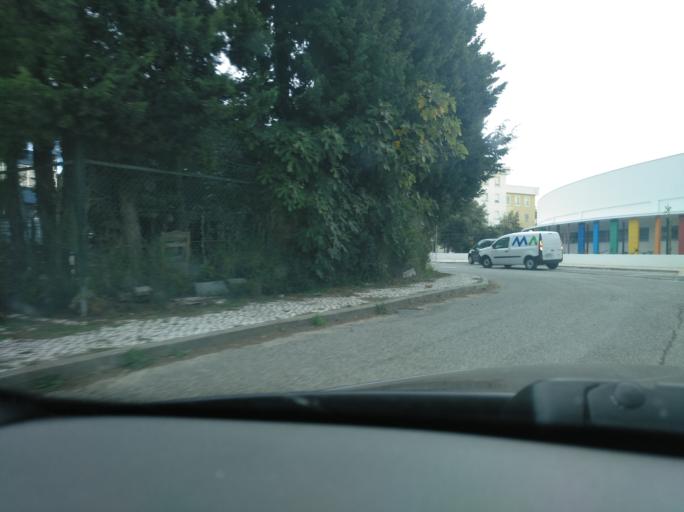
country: PT
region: Lisbon
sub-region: Amadora
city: Amadora
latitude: 38.7350
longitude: -9.2117
